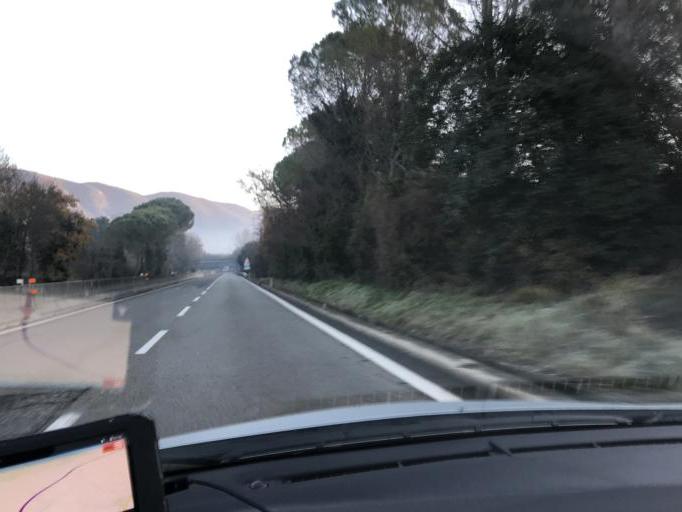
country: IT
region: Umbria
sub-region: Provincia di Terni
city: Terni
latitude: 42.5792
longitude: 12.6358
